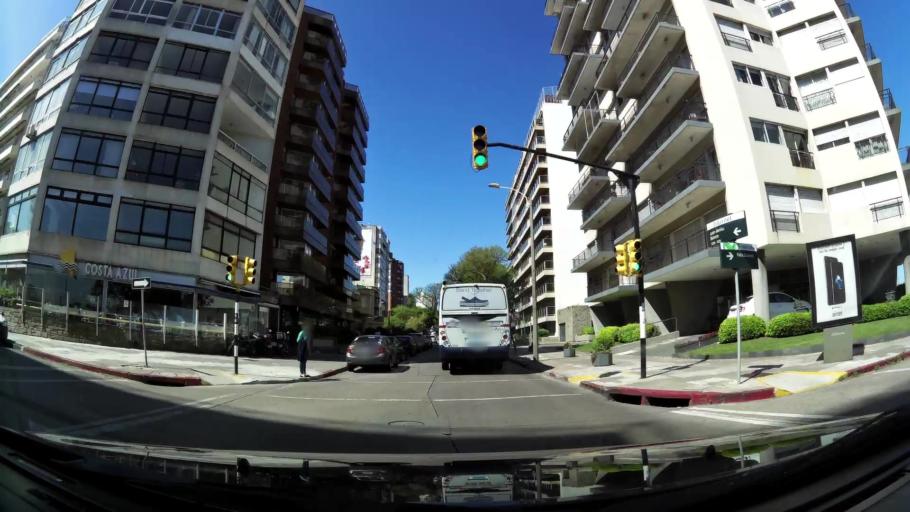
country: UY
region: Montevideo
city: Montevideo
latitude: -34.9091
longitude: -56.1430
